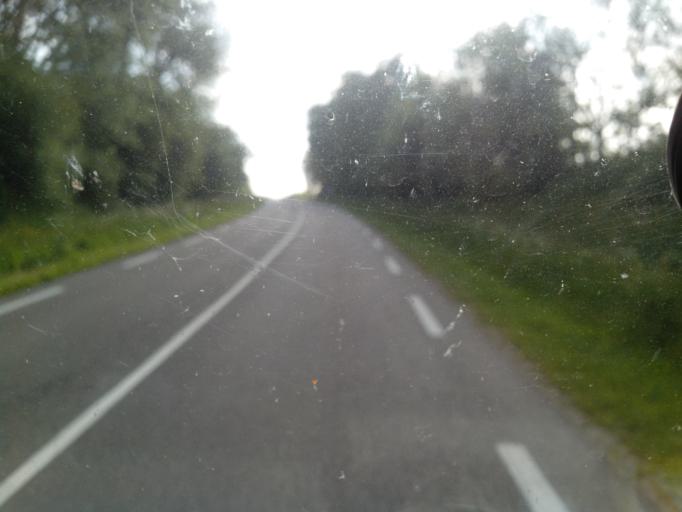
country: FR
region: Haute-Normandie
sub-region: Departement de la Seine-Maritime
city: Totes
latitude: 49.6755
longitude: 1.1045
